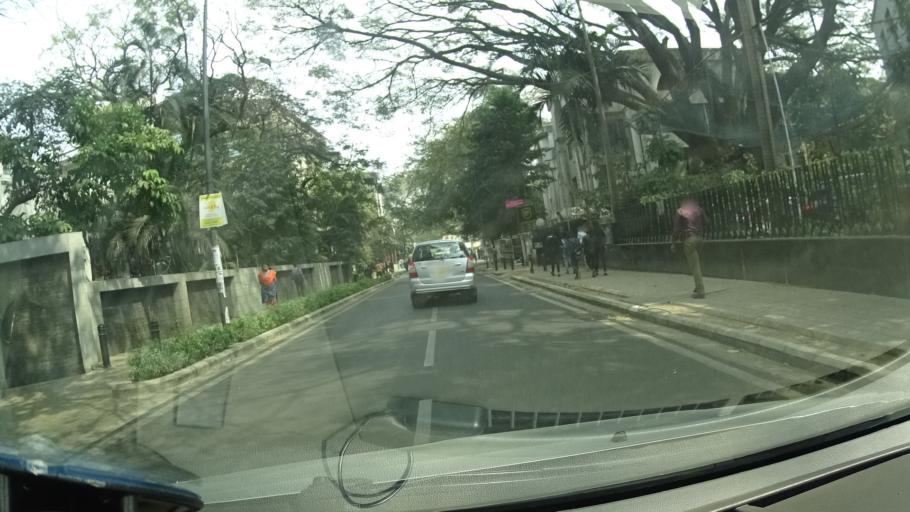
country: IN
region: Karnataka
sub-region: Bangalore Urban
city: Bangalore
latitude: 12.9904
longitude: 77.5909
